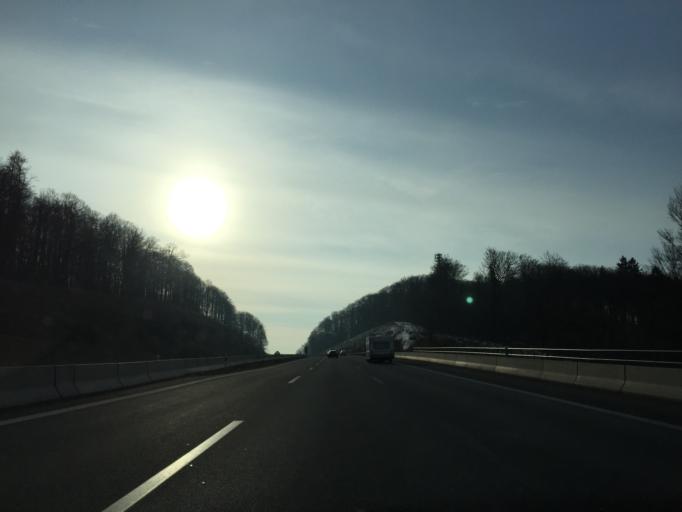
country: DE
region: Bavaria
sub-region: Regierungsbezirk Unterfranken
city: Schollbrunn
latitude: 49.8744
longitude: 9.4457
